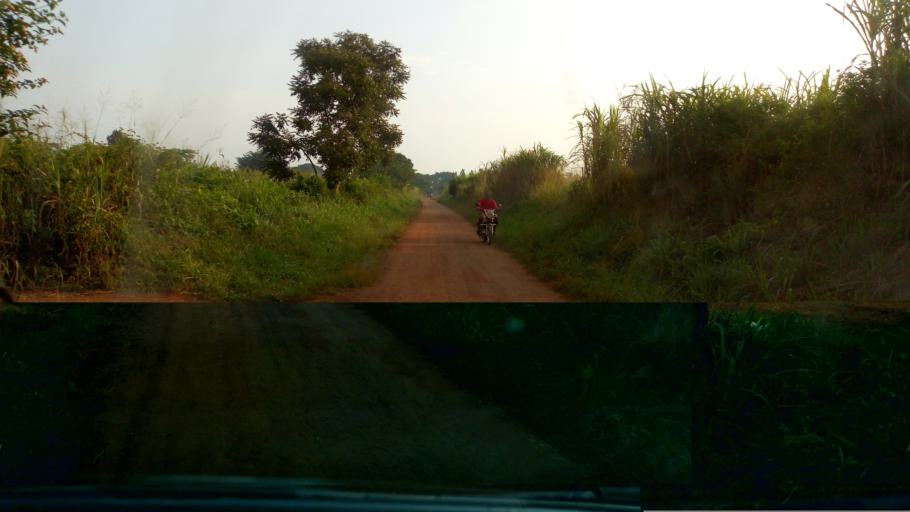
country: UG
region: Western Region
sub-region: Masindi District
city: Masindi
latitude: 1.7685
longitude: 31.8396
